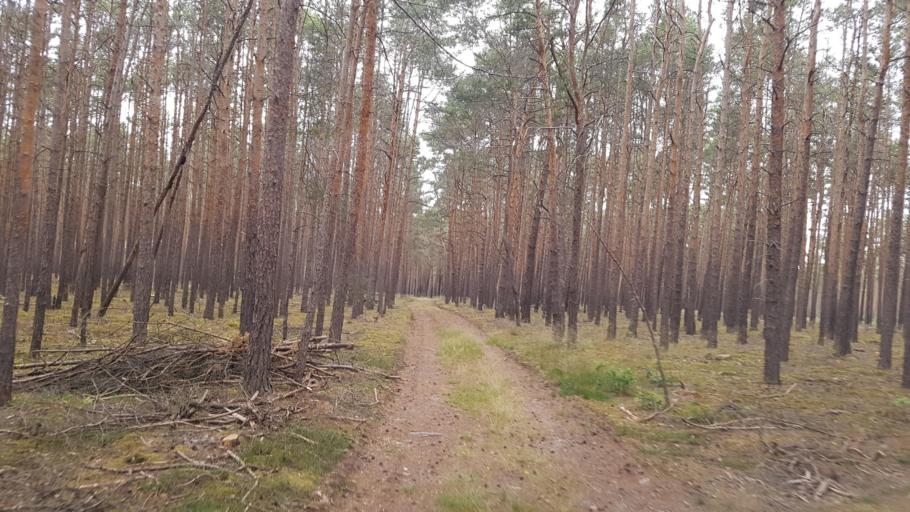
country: DE
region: Brandenburg
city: Schonborn
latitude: 51.6794
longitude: 13.4751
